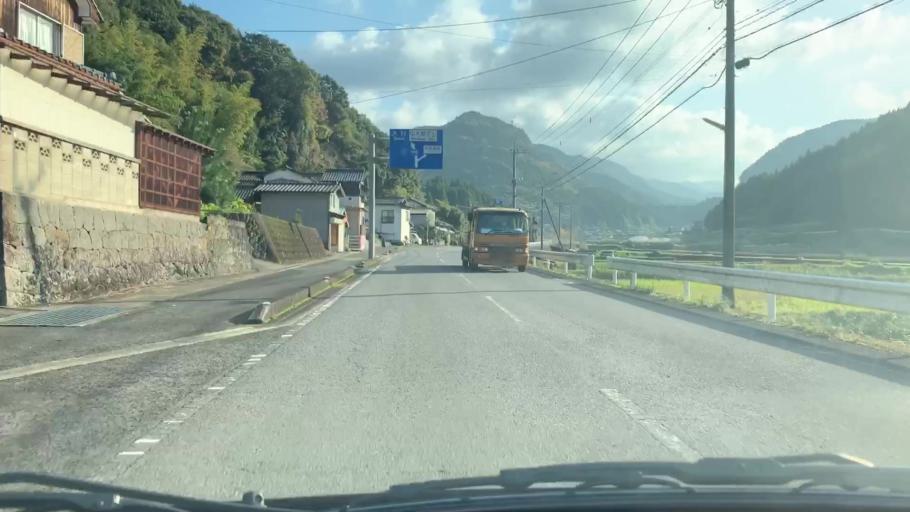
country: JP
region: Saga Prefecture
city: Kashima
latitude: 33.0588
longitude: 130.0702
